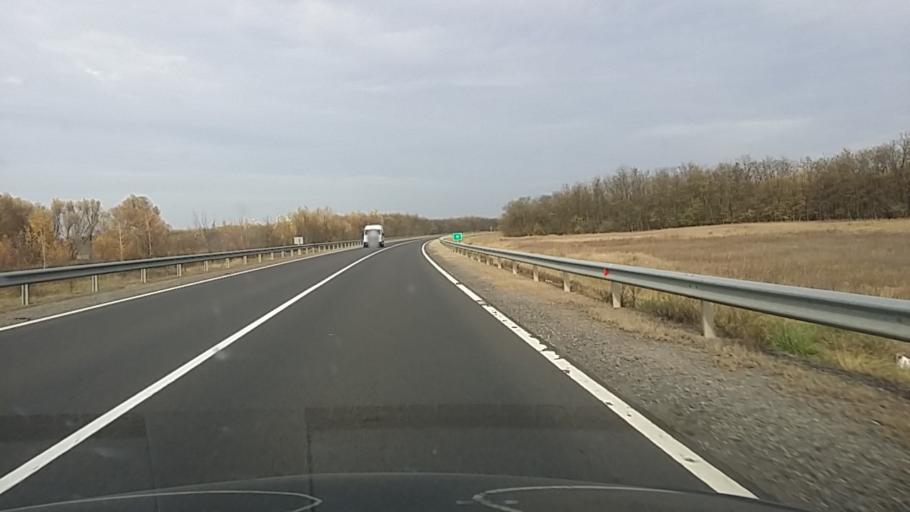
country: HU
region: Szabolcs-Szatmar-Bereg
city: Nyirpazony
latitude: 47.9899
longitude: 21.8220
